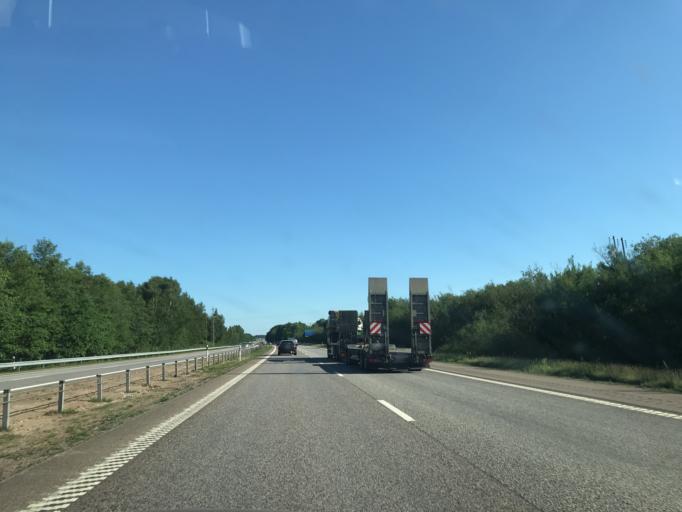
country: SE
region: Halland
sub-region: Halmstads Kommun
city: Halmstad
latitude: 56.6936
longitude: 12.8943
